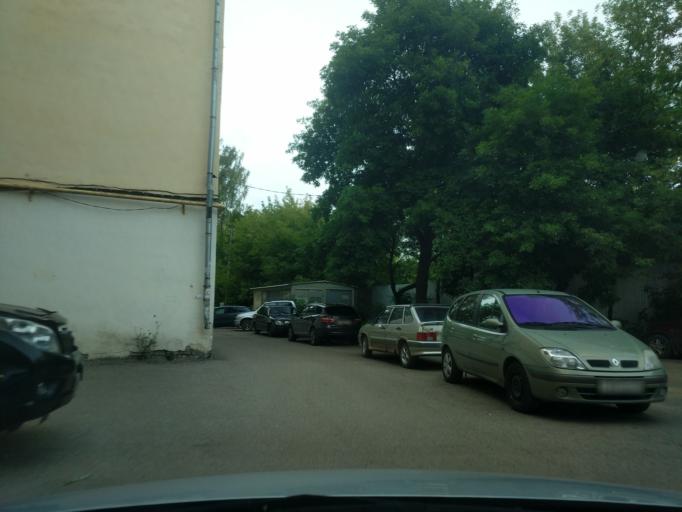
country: RU
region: Kirov
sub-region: Kirovo-Chepetskiy Rayon
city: Kirov
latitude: 58.6087
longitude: 49.6580
